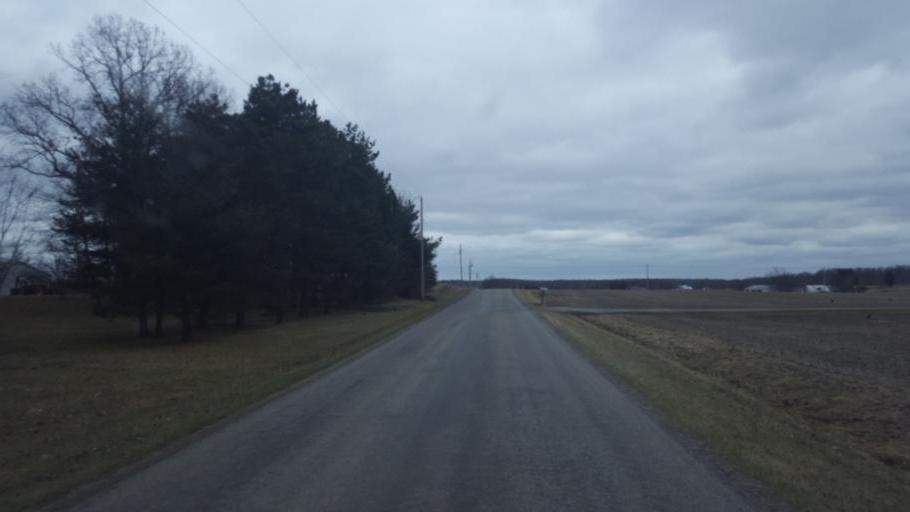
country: US
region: Ohio
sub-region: Crawford County
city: Galion
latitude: 40.6676
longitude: -82.7212
